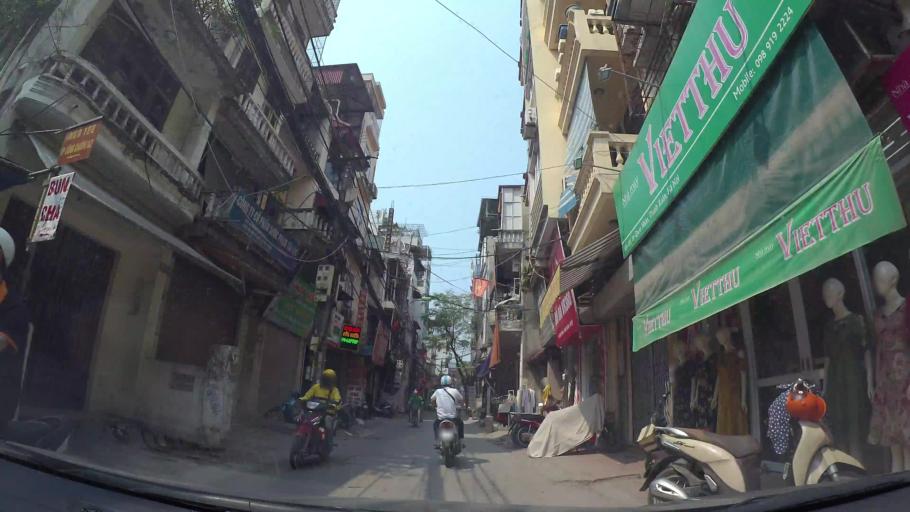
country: VN
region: Ha Noi
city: Thanh Xuan
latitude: 21.0058
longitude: 105.8117
